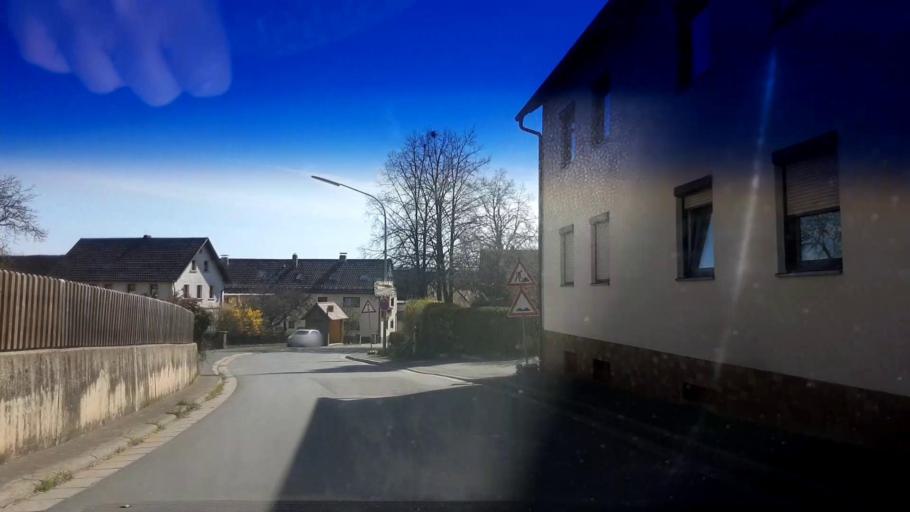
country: DE
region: Bavaria
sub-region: Upper Franconia
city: Bindlach
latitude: 50.0132
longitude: 11.6228
